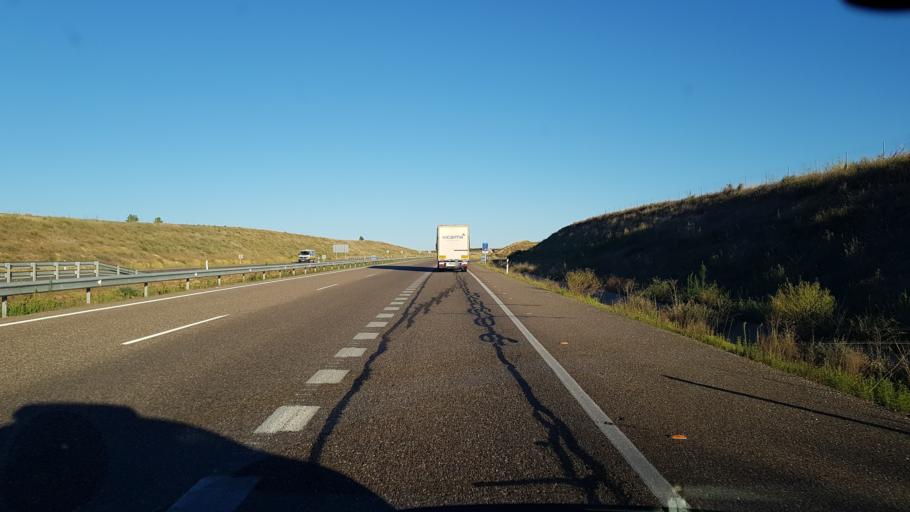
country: ES
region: Castille and Leon
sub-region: Provincia de Zamora
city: Valcabado
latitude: 41.5543
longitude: -5.7381
